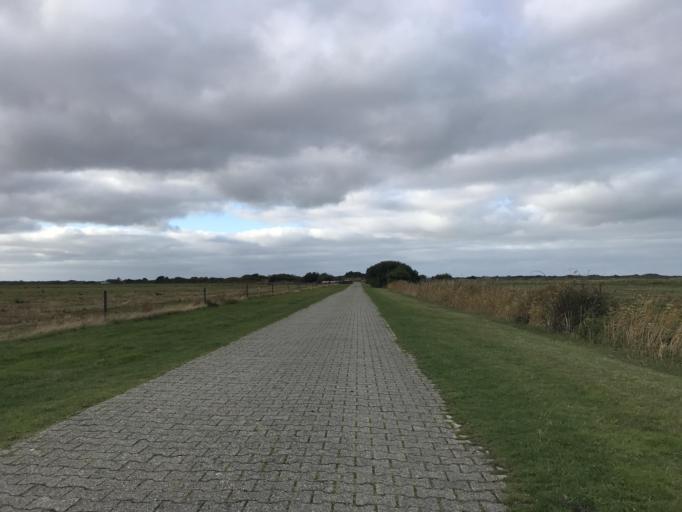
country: DE
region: Lower Saxony
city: Borkum
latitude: 53.5963
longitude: 6.7385
